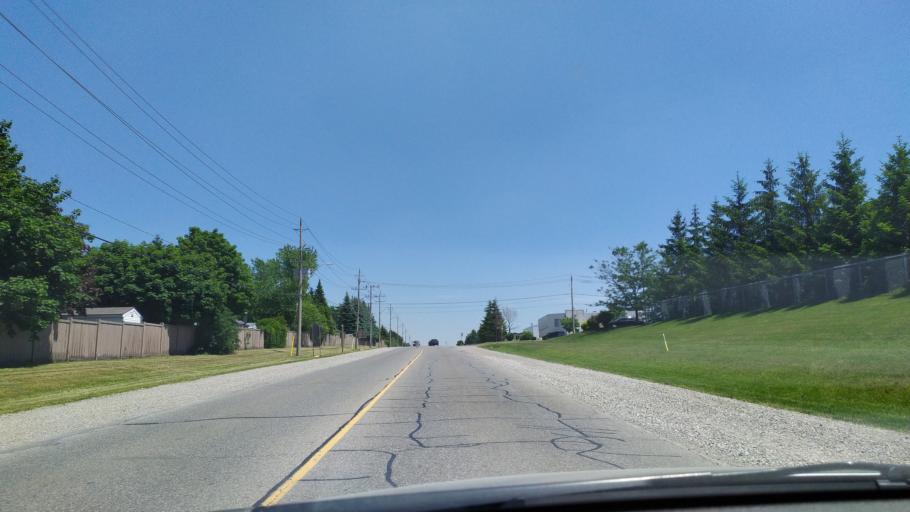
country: CA
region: Ontario
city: Kitchener
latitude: 43.4027
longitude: -80.4942
